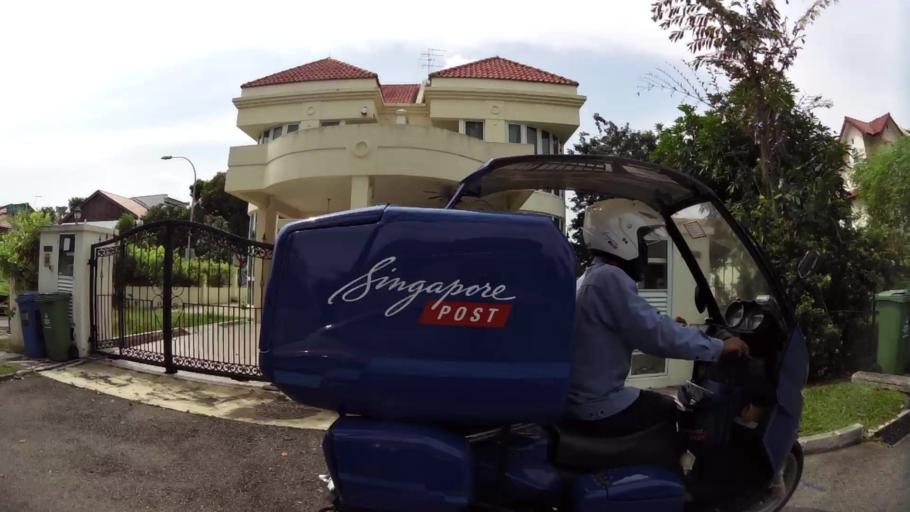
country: MY
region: Johor
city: Kampung Pasir Gudang Baru
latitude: 1.3650
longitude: 103.9741
